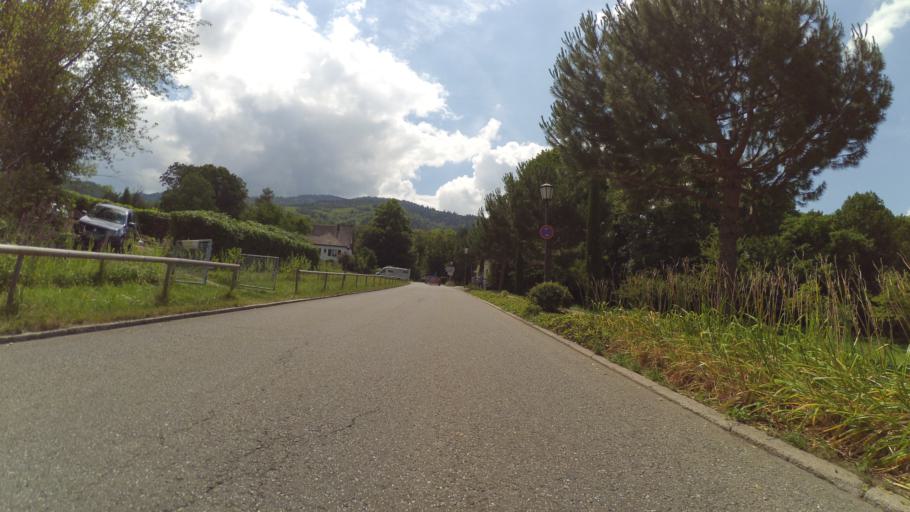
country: DE
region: Baden-Wuerttemberg
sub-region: Freiburg Region
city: Badenweiler
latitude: 47.8071
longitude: 7.6788
